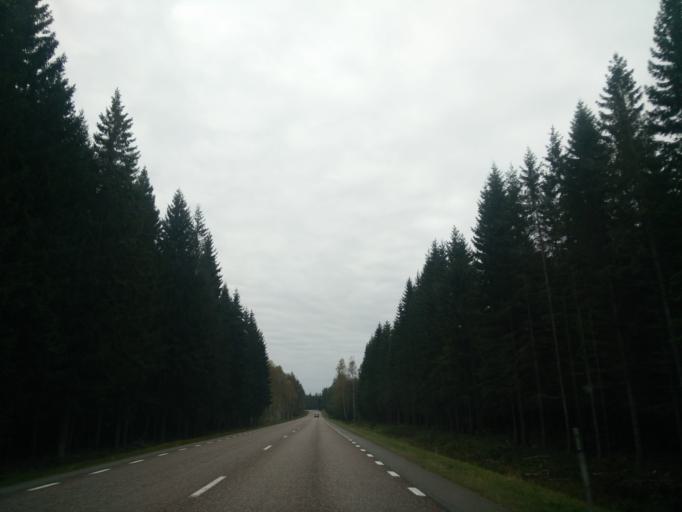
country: SE
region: Gaevleborg
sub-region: Gavle Kommun
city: Norrsundet
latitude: 60.8430
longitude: 17.1993
